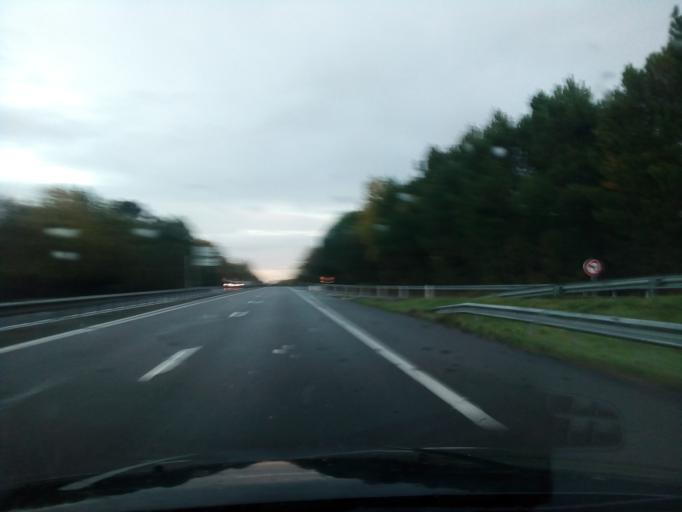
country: FR
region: Aquitaine
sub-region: Departement de la Gironde
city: Gauriaguet
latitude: 45.0677
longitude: -0.3918
